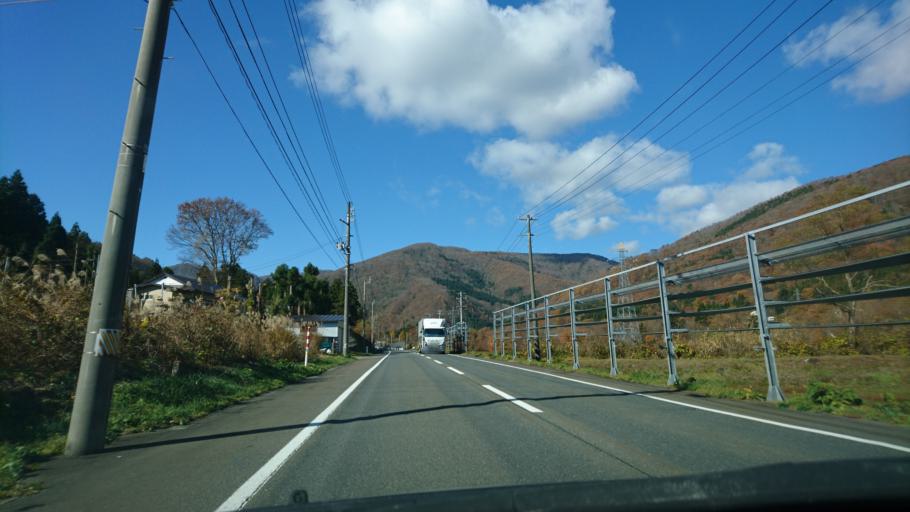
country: JP
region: Iwate
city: Kitakami
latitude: 39.3076
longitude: 140.9167
